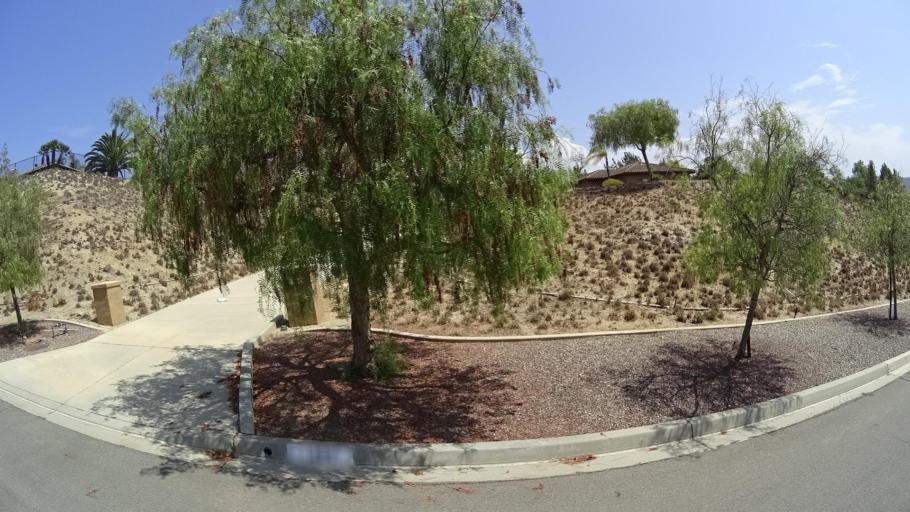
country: US
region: California
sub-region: San Diego County
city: Bonsall
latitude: 33.3127
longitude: -117.2029
